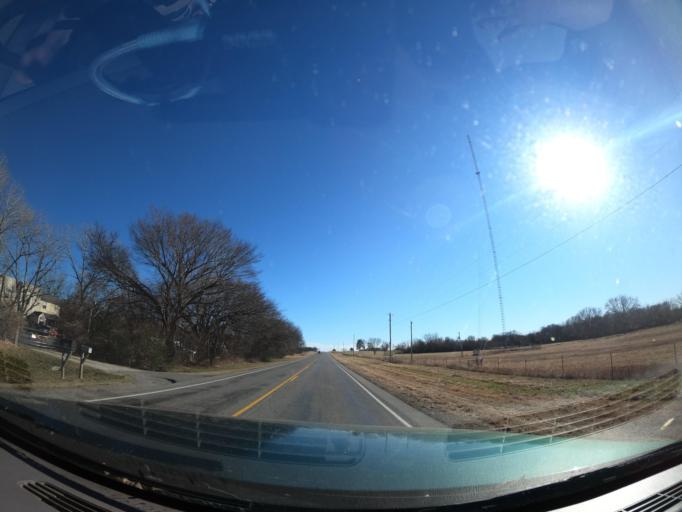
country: US
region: Oklahoma
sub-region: Muskogee County
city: Haskell
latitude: 35.7678
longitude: -95.6517
